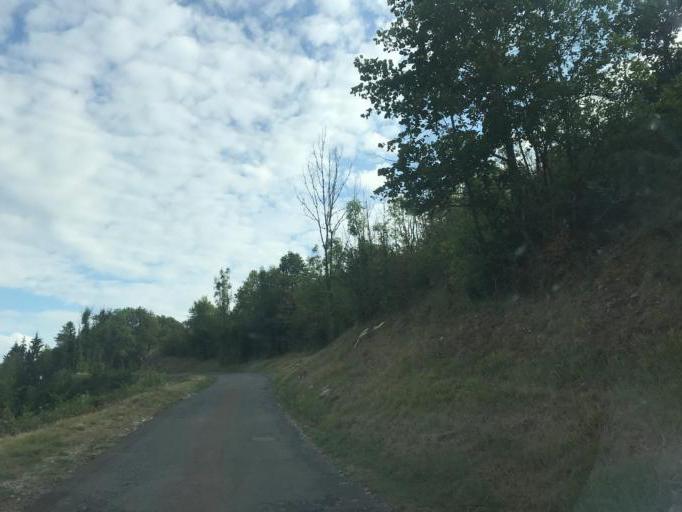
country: FR
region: Franche-Comte
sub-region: Departement du Jura
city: Saint-Lupicin
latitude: 46.4309
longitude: 5.8056
